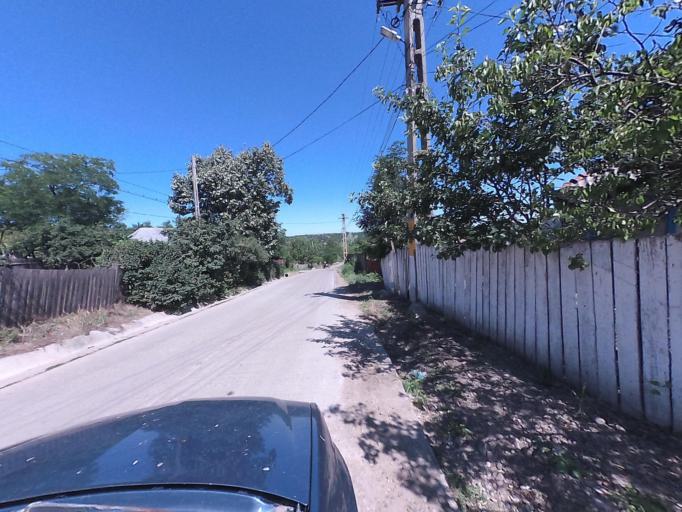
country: RO
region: Vaslui
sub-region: Comuna Costesti
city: Costesti
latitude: 46.4923
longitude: 27.7681
